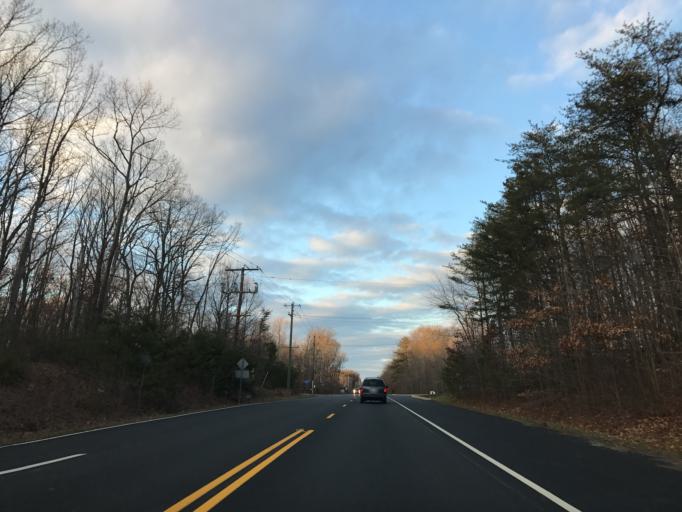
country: US
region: Maryland
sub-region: Cecil County
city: North East
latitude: 39.5803
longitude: -75.9433
